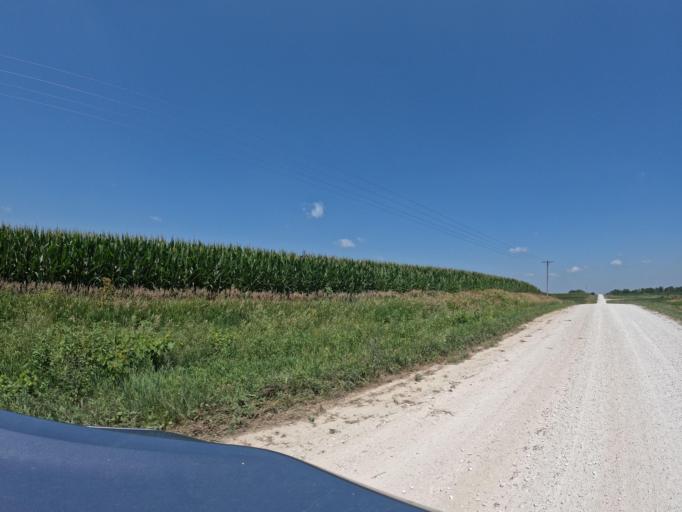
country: US
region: Iowa
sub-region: Keokuk County
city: Sigourney
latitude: 41.2769
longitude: -92.2381
